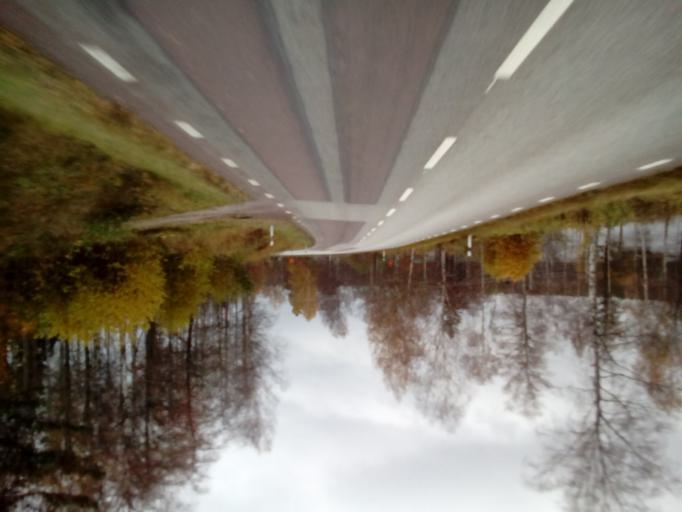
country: SE
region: OErebro
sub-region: Degerfors Kommun
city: Degerfors
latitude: 59.1217
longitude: 14.5251
